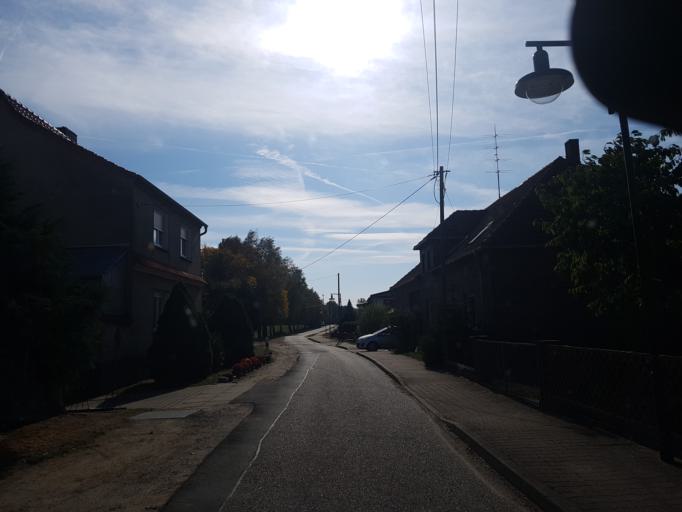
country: DE
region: Brandenburg
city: Hohenbucko
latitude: 51.6968
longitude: 13.4640
